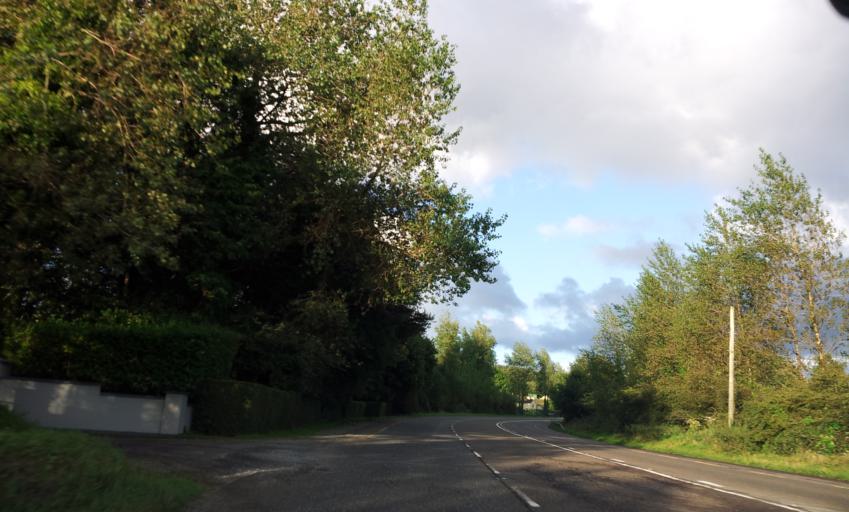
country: IE
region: Munster
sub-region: Ciarrai
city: Castleisland
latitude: 52.2654
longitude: -9.4456
